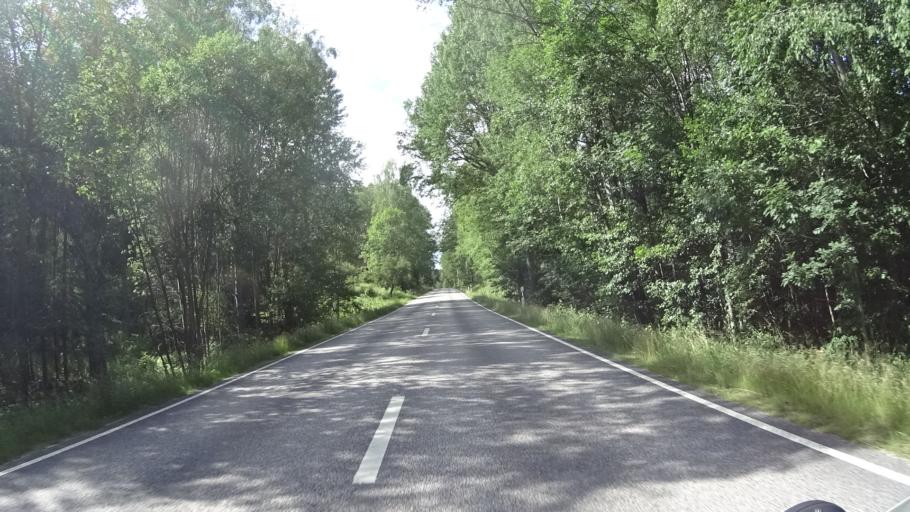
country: SE
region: Kalmar
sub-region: Vasterviks Kommun
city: Overum
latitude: 58.0768
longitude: 16.1866
